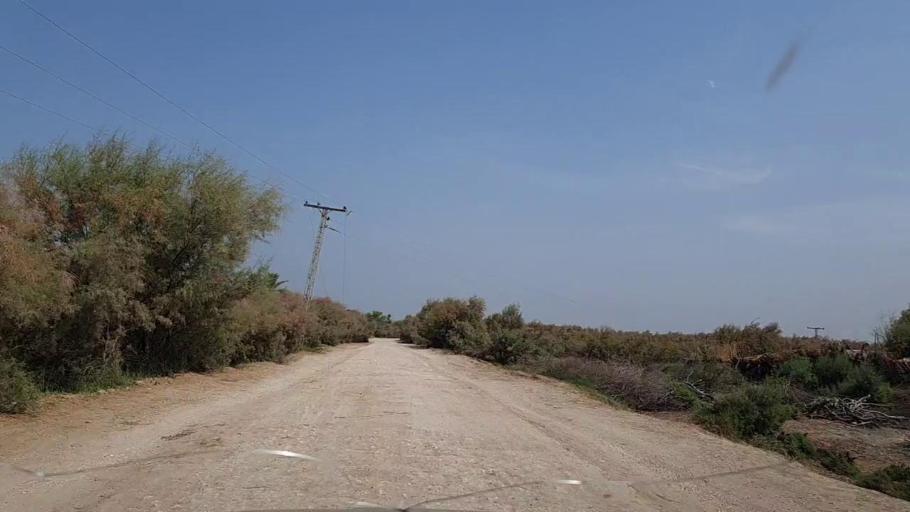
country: PK
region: Sindh
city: Adilpur
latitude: 27.8255
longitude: 69.2998
